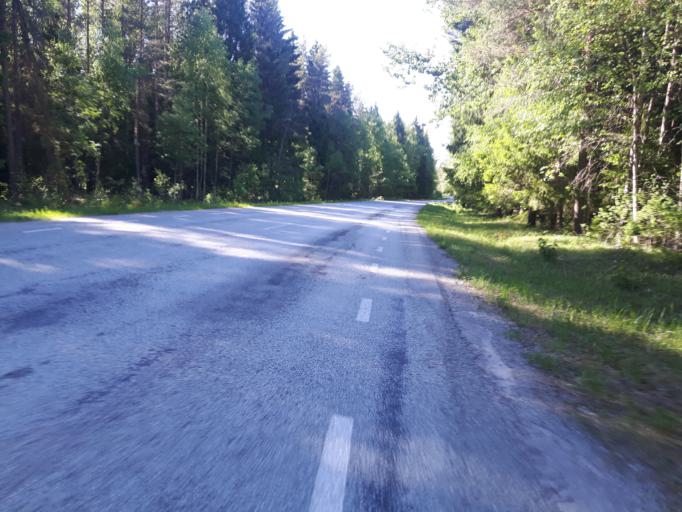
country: EE
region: Laeaene-Virumaa
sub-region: Kadrina vald
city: Kadrina
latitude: 59.5458
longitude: 26.0214
